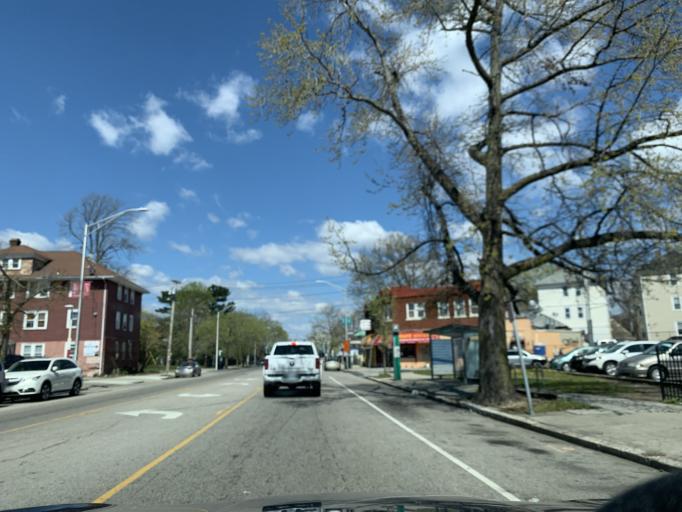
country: US
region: Rhode Island
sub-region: Providence County
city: Providence
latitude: 41.7918
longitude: -71.4067
